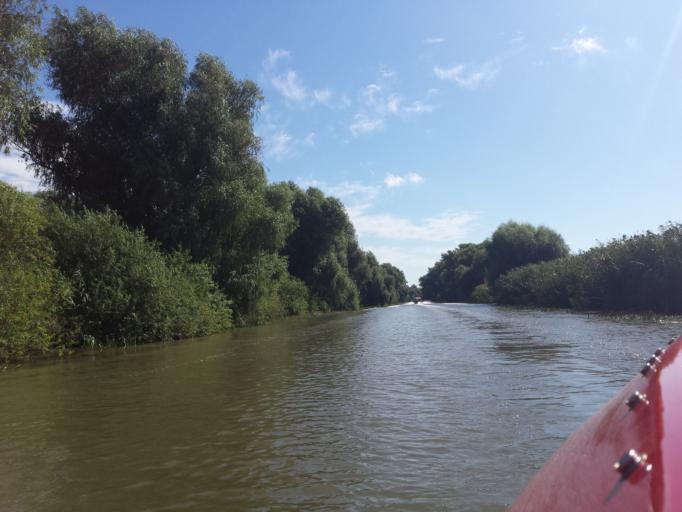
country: RO
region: Tulcea
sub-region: Comuna Mahmudia
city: Mahmudia
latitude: 45.2386
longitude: 29.1189
